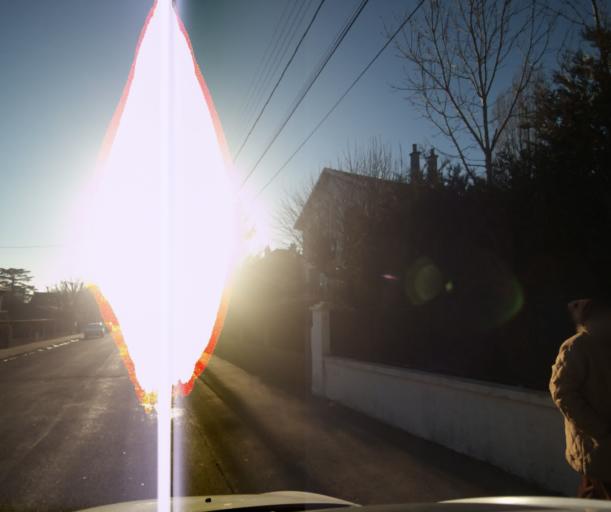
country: FR
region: Franche-Comte
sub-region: Departement du Doubs
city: Besancon
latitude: 47.2595
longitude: 6.0357
